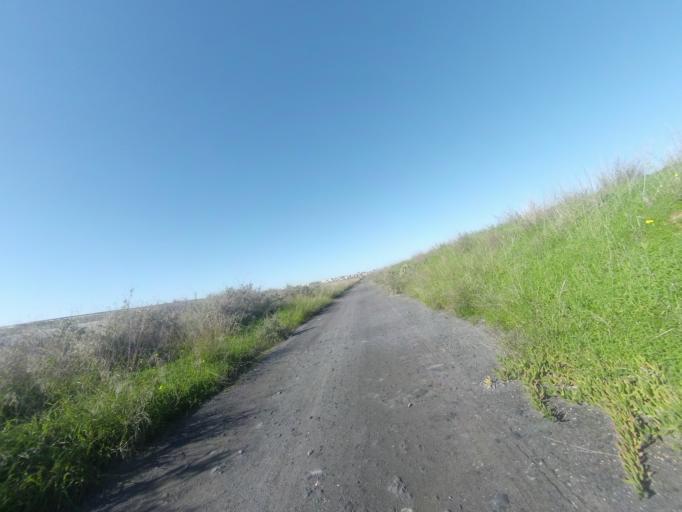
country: ES
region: Andalusia
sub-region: Provincia de Huelva
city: Palos de la Frontera
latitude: 37.2535
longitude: -6.9070
